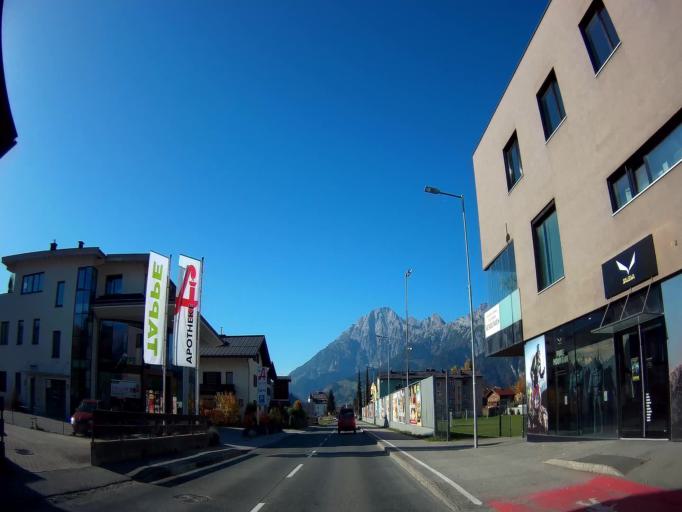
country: AT
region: Salzburg
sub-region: Politischer Bezirk Zell am See
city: Saalfelden am Steinernen Meer
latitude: 47.4299
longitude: 12.8404
